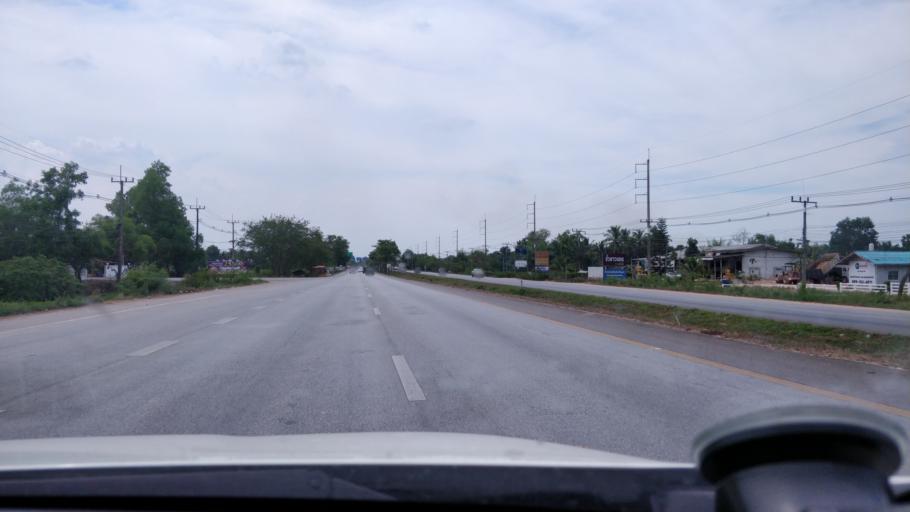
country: TH
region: Surat Thani
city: Phunphin
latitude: 9.0898
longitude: 99.1677
